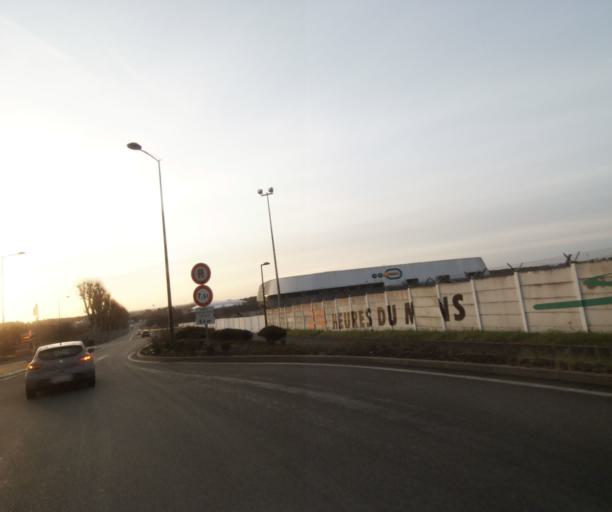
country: FR
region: Pays de la Loire
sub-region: Departement de la Sarthe
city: Le Mans
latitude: 47.9619
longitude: 0.2231
